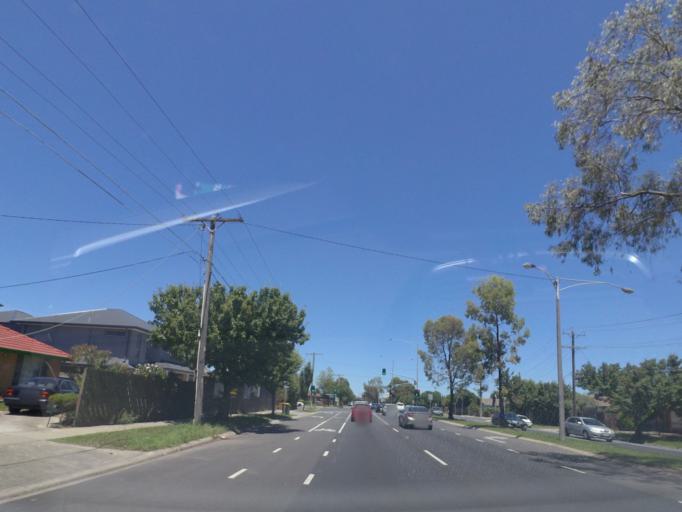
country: AU
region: Victoria
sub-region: Whittlesea
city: Thomastown
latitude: -37.6813
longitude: 145.0298
